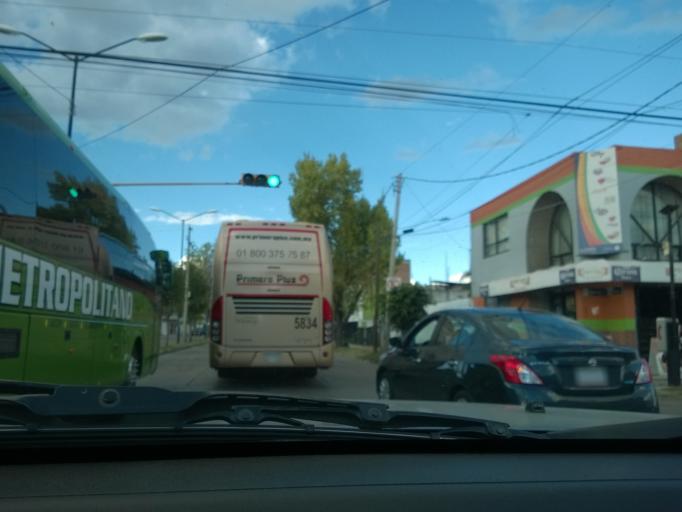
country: MX
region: Guanajuato
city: Leon
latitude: 21.1191
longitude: -101.6580
